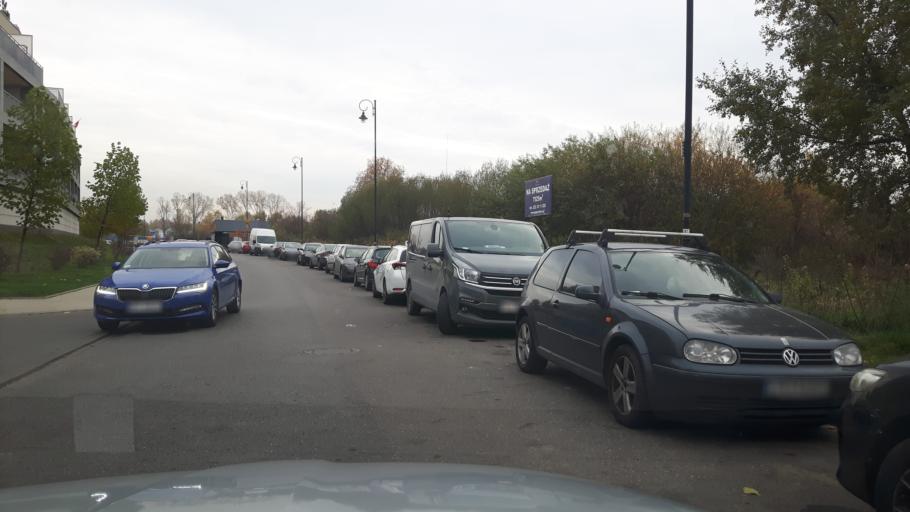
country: PL
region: Masovian Voivodeship
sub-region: Warszawa
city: Ursynow
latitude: 52.1613
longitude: 21.0639
